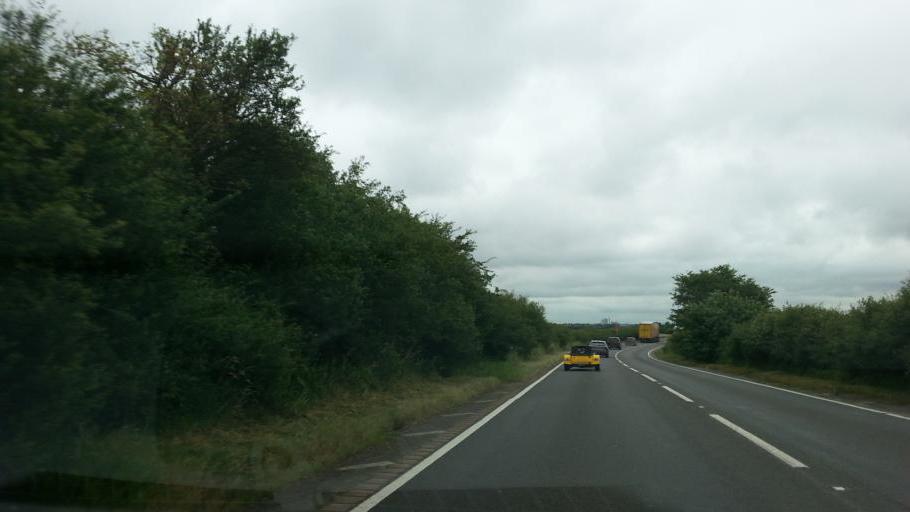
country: GB
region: England
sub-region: District of Rutland
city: Ketton
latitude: 52.5820
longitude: -0.5608
